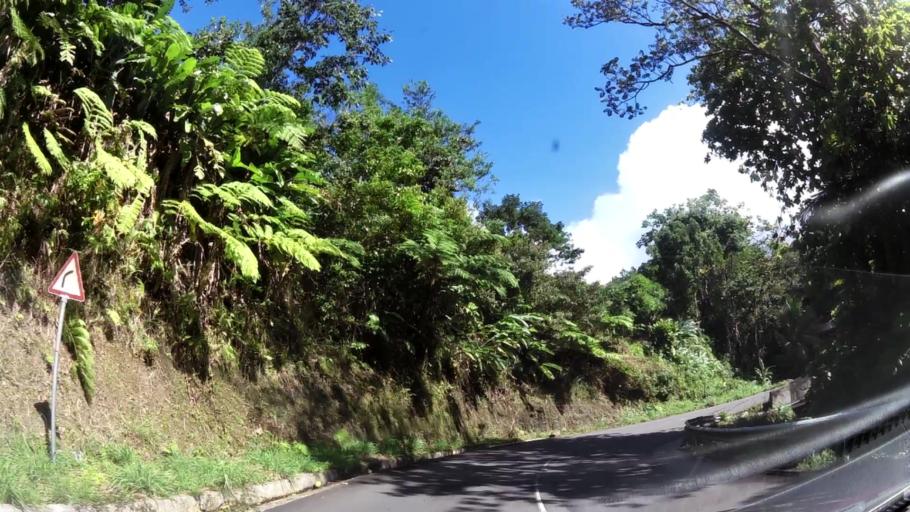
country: DM
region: Saint Paul
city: Pont Casse
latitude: 15.3639
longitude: -61.3532
